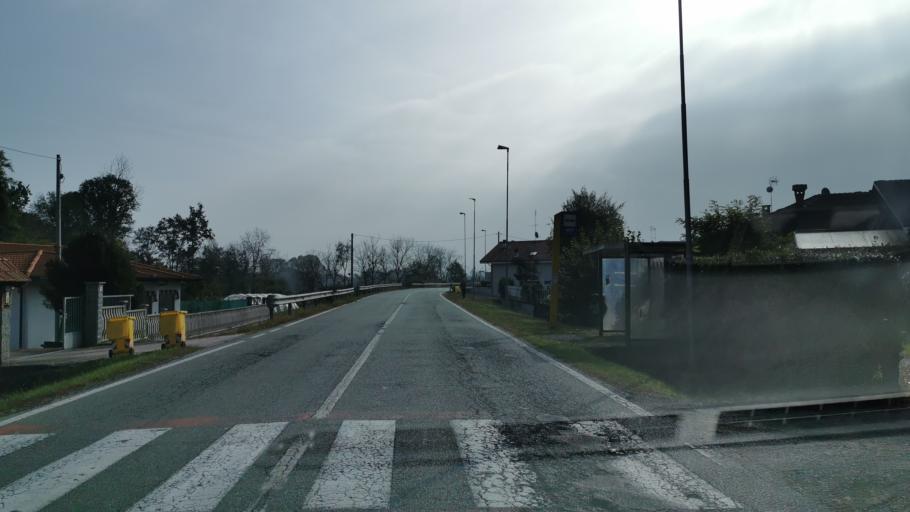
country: IT
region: Piedmont
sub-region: Provincia di Torino
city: Front
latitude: 45.2664
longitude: 7.6900
